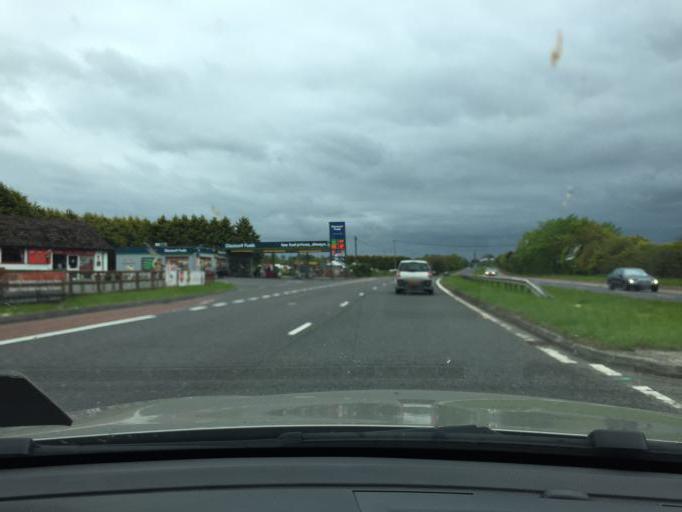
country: GB
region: Northern Ireland
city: Hillsborough
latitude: 54.4430
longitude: -6.1137
